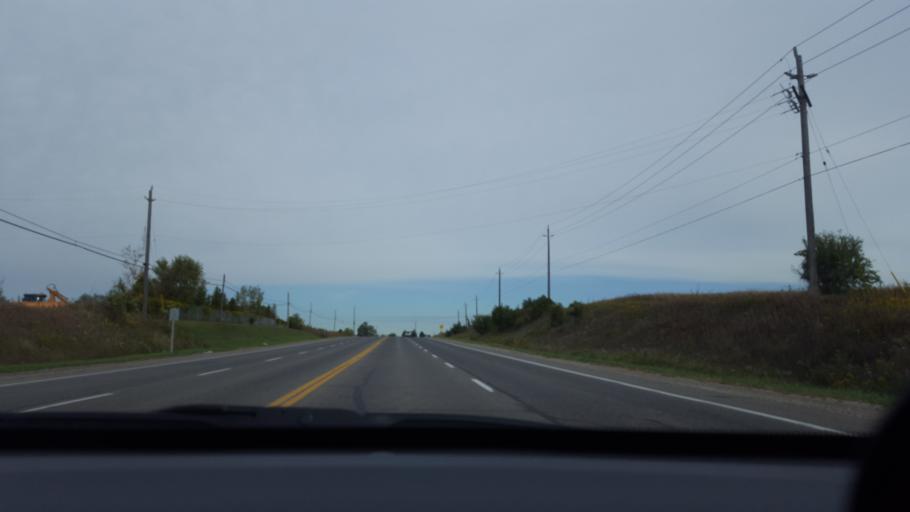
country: CA
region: Ontario
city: Vaughan
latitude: 43.9022
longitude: -79.5233
